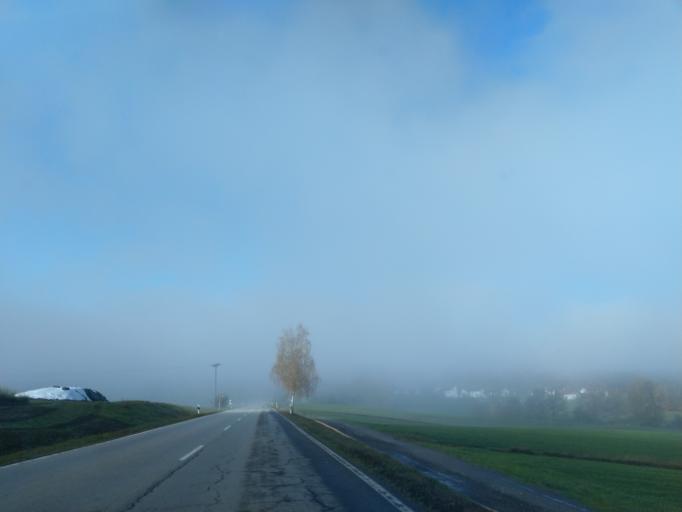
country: DE
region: Bavaria
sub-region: Lower Bavaria
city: Aussernzell
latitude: 48.7202
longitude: 13.2373
